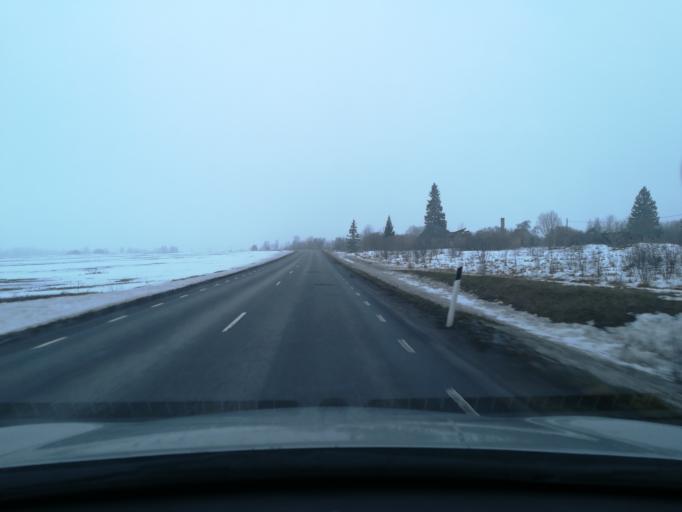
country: EE
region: Harju
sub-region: Raasiku vald
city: Raasiku
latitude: 59.3587
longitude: 25.1497
